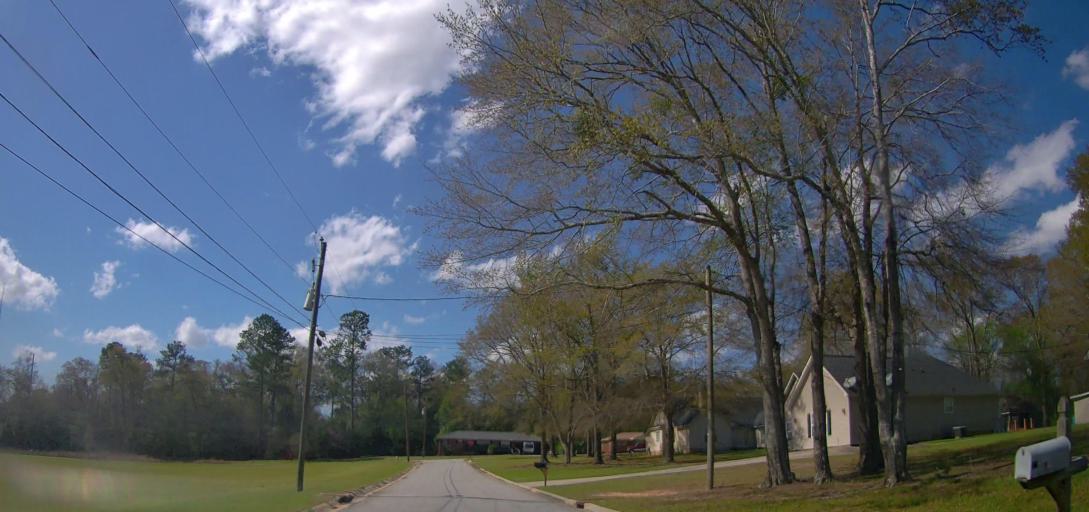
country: US
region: Georgia
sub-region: Bibb County
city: Macon
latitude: 32.8058
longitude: -83.5357
